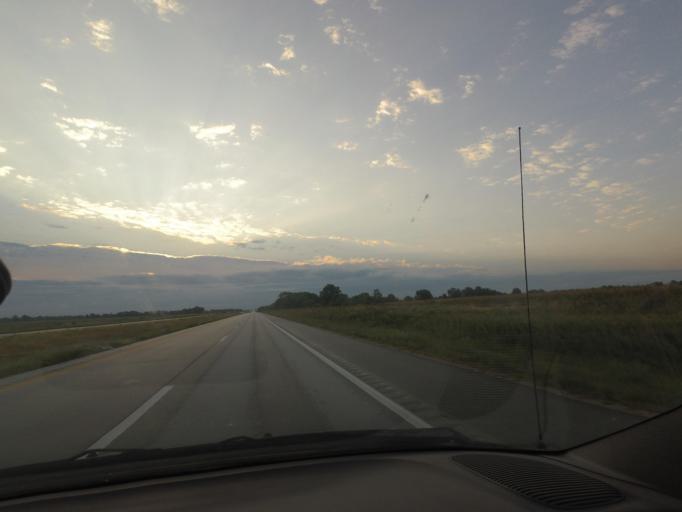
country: US
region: Missouri
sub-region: Shelby County
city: Shelbina
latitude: 39.7366
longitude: -92.2242
